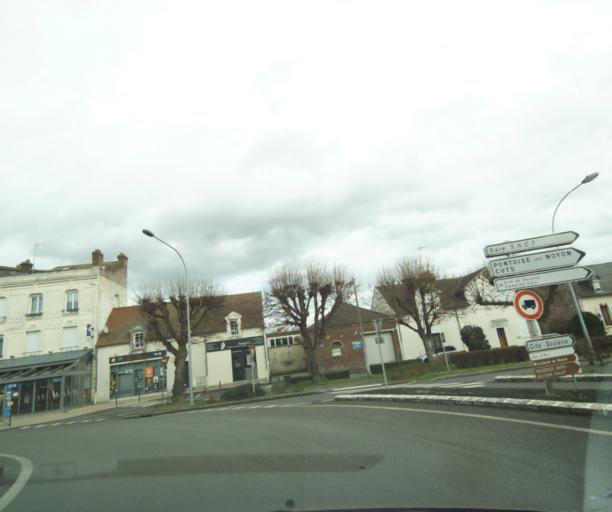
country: FR
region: Picardie
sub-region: Departement de l'Oise
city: Noyon
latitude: 49.5783
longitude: 2.9947
